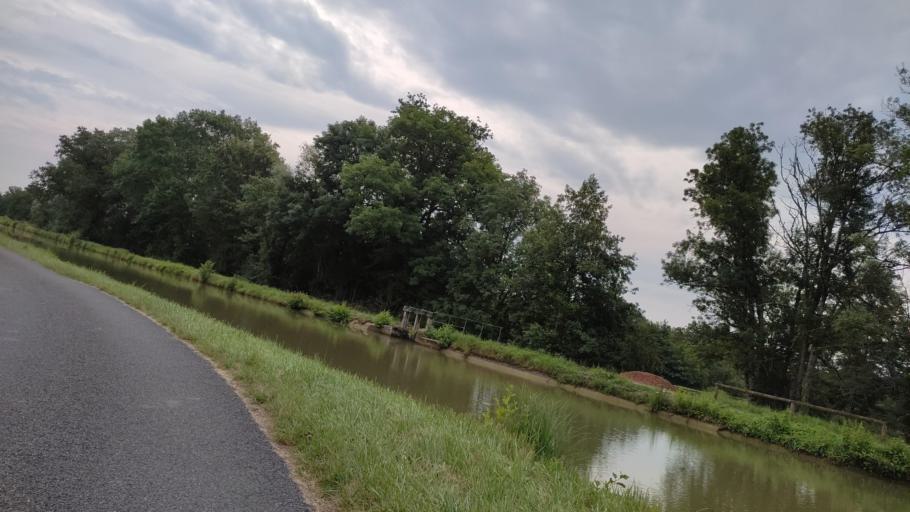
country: FR
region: Bourgogne
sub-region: Departement de la Nievre
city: Cercy-la-Tour
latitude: 46.8689
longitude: 3.6499
